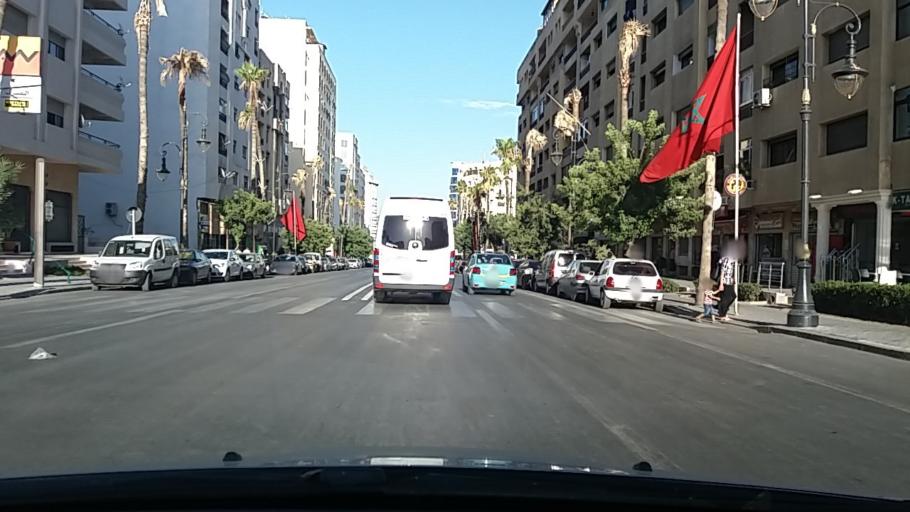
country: MA
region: Tanger-Tetouan
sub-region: Tanger-Assilah
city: Tangier
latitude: 35.7704
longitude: -5.8080
